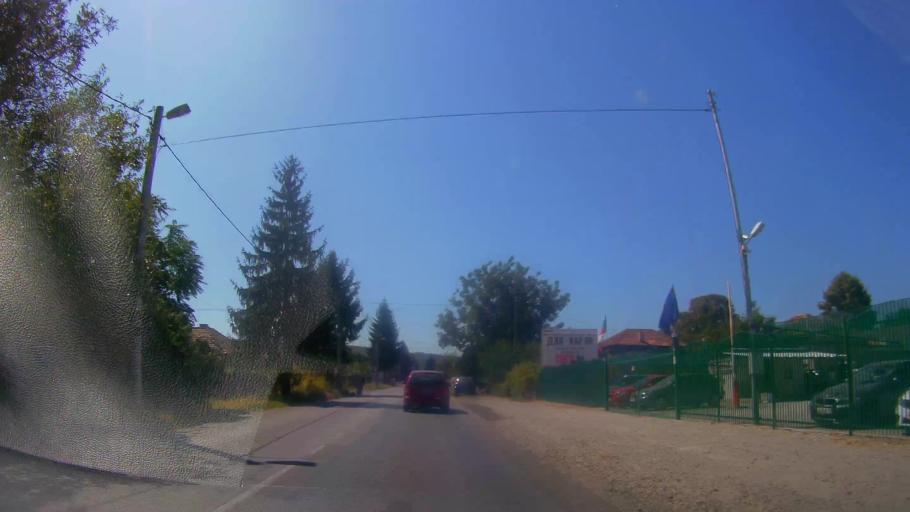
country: BG
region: Veliko Turnovo
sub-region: Obshtina Gorna Oryakhovitsa
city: Purvomaytsi
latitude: 43.1474
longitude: 25.6141
